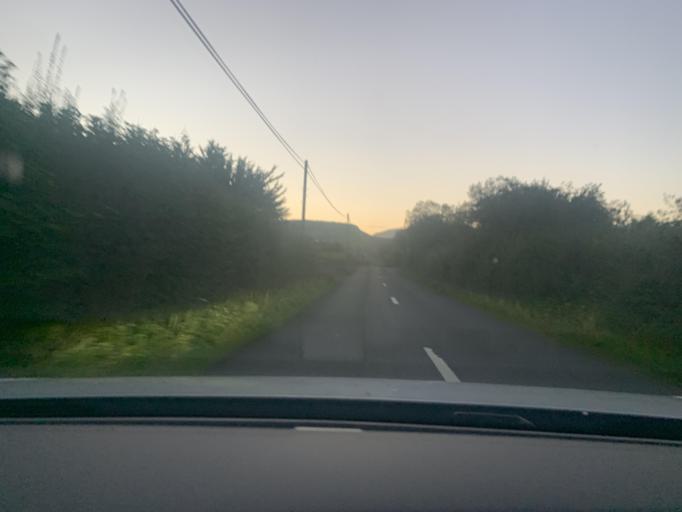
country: IE
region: Connaught
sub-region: County Leitrim
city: Manorhamilton
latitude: 54.2759
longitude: -8.2934
